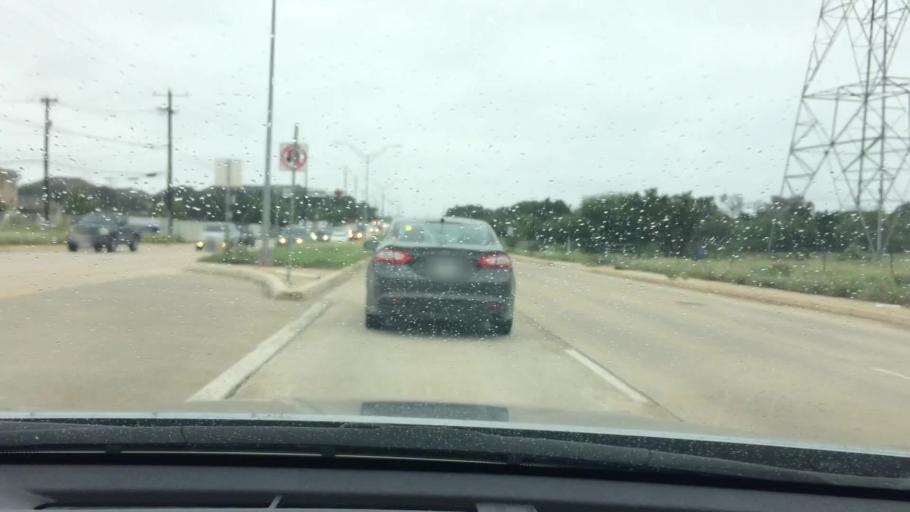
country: US
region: Texas
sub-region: Bexar County
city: Hollywood Park
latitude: 29.6360
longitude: -98.4241
